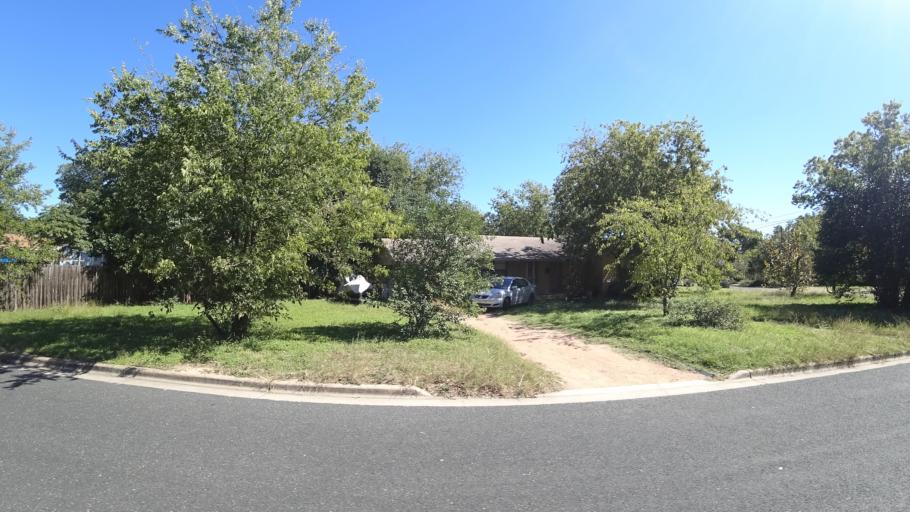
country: US
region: Texas
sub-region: Travis County
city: Austin
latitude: 30.3371
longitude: -97.7382
